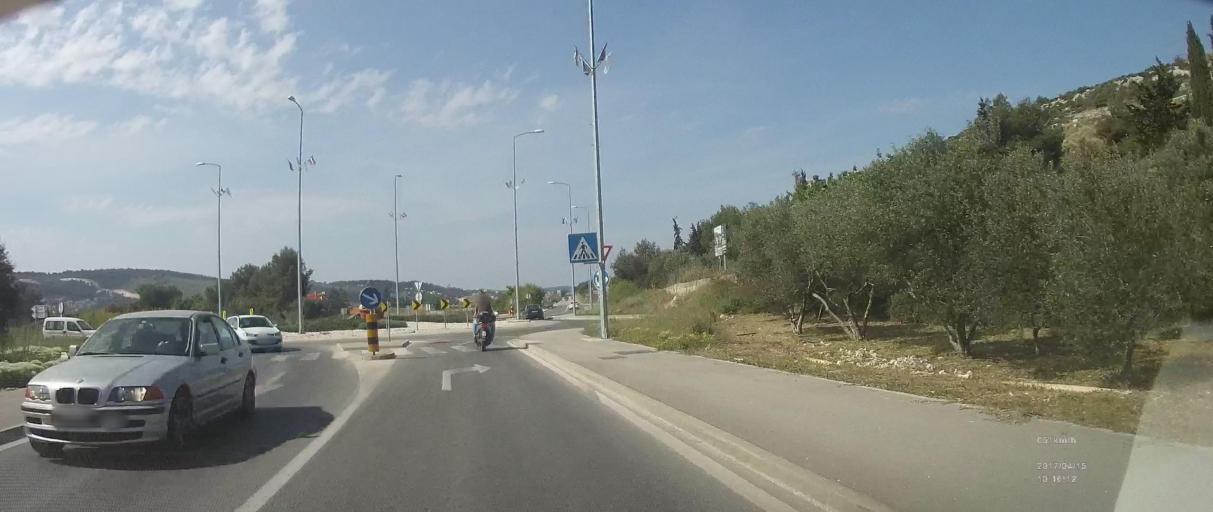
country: HR
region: Splitsko-Dalmatinska
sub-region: Grad Trogir
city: Trogir
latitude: 43.5315
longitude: 16.2791
